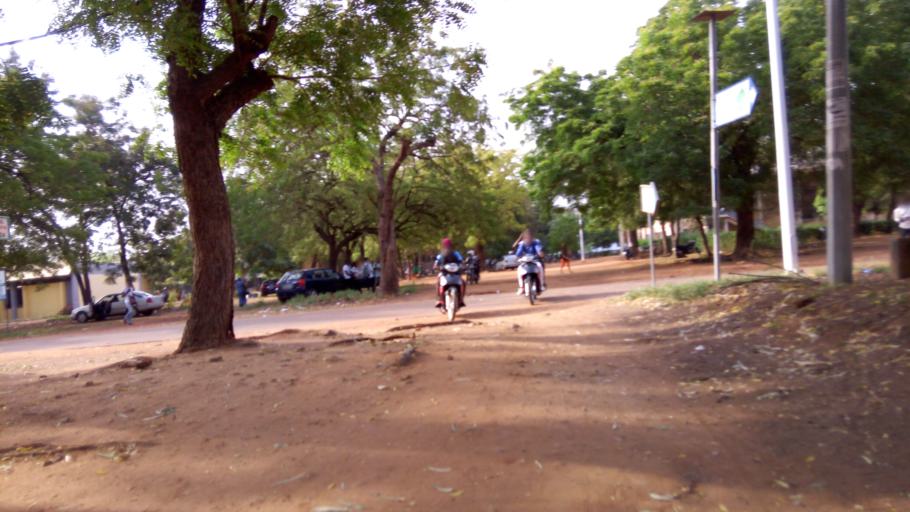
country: TG
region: Maritime
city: Lome
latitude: 6.1744
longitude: 1.2136
